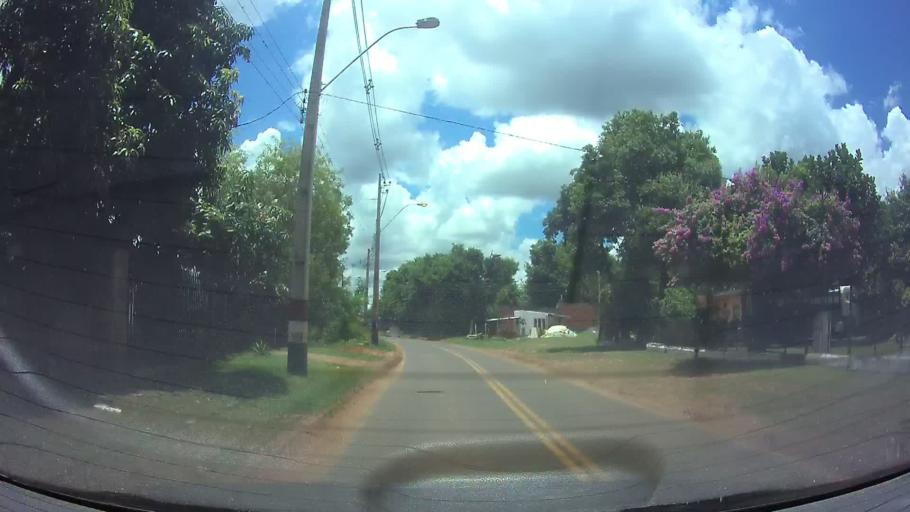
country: PY
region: Central
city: Capiata
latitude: -25.3208
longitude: -57.4282
